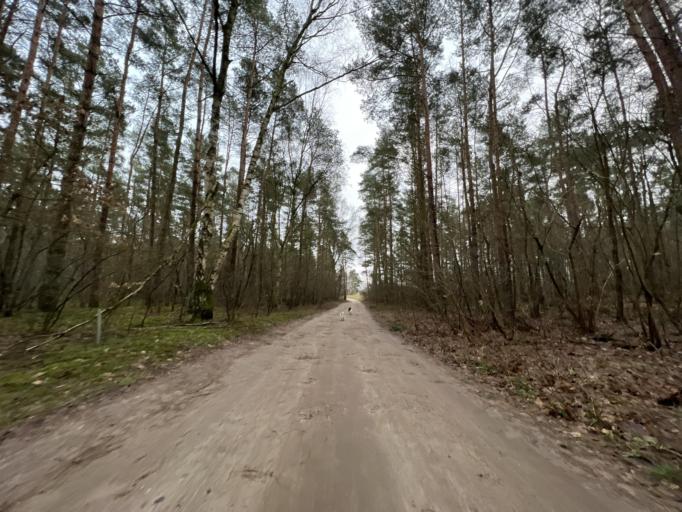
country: DE
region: Mecklenburg-Vorpommern
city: Plau am See
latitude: 53.4938
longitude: 12.2750
